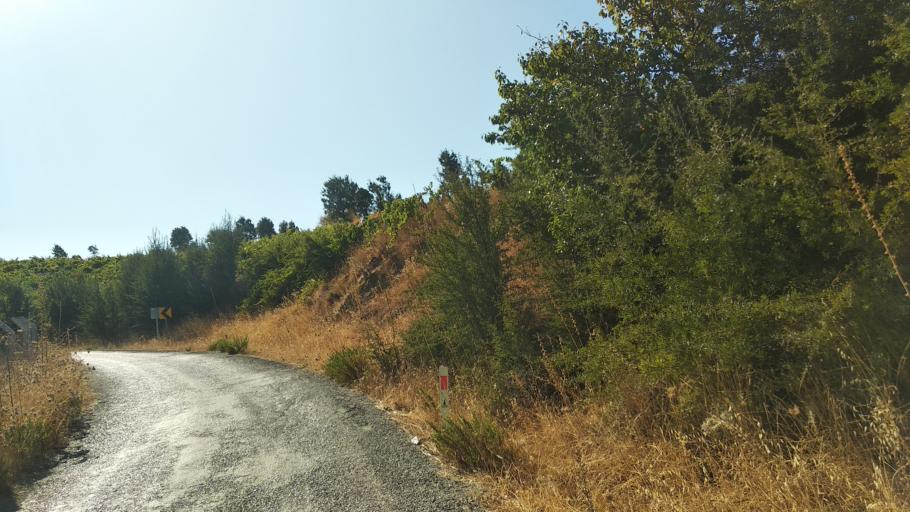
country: TR
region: Izmir
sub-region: Seferihisar
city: Seferhisar
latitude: 38.3263
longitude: 26.9548
